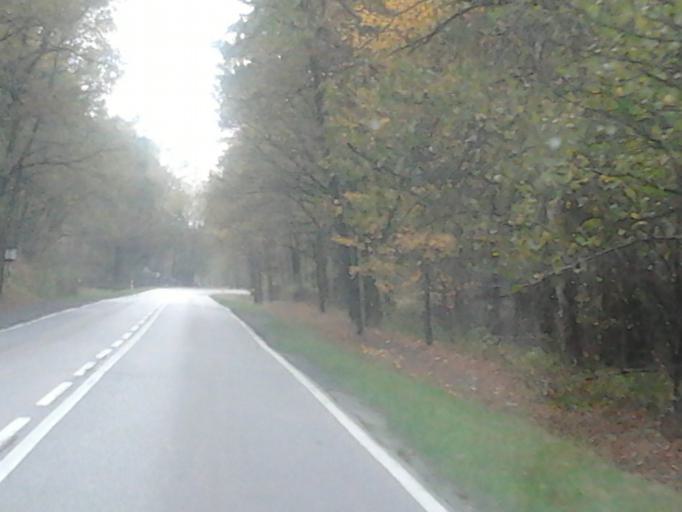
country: PL
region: Masovian Voivodeship
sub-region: Powiat pruszkowski
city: Nadarzyn
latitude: 52.0999
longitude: 20.8510
